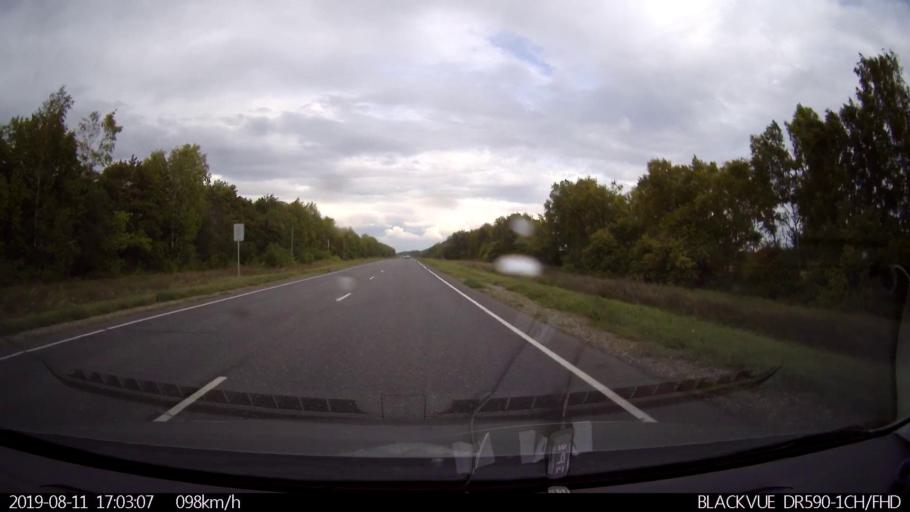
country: RU
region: Ulyanovsk
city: Mayna
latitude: 54.3040
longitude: 47.7316
